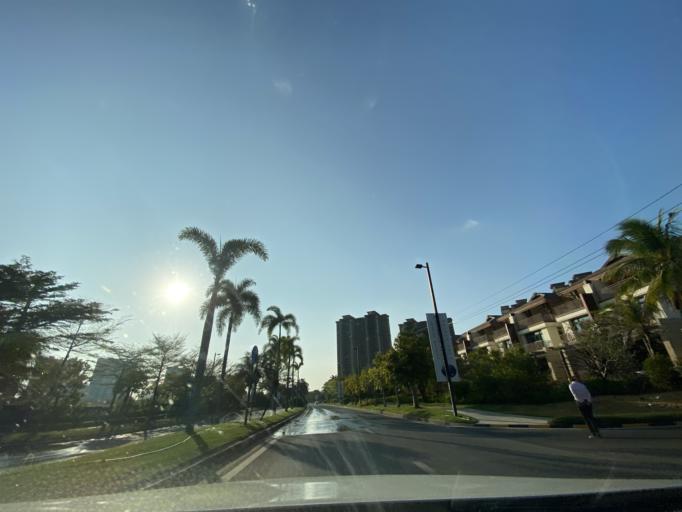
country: CN
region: Hainan
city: Xincun
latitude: 18.4240
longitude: 109.9343
